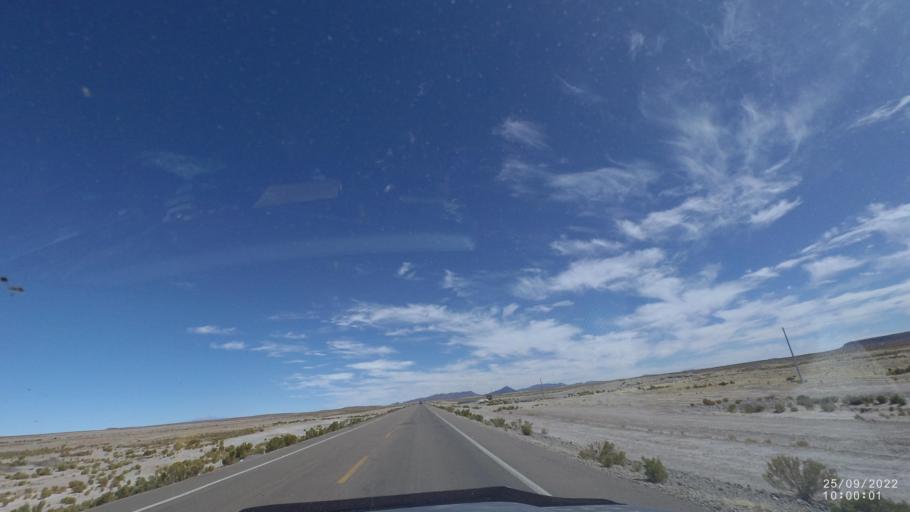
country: BO
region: Potosi
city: Colchani
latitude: -20.2810
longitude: -66.9431
